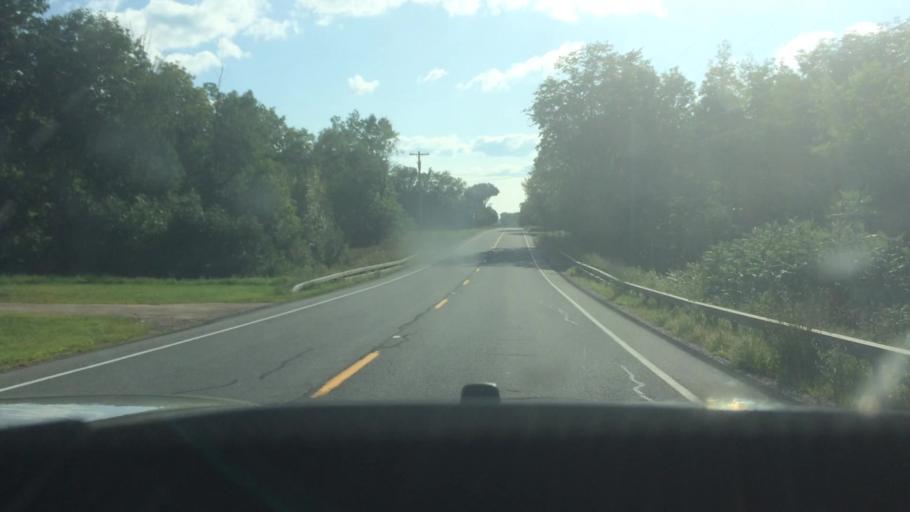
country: US
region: New York
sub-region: Franklin County
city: Malone
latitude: 44.7463
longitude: -74.5691
